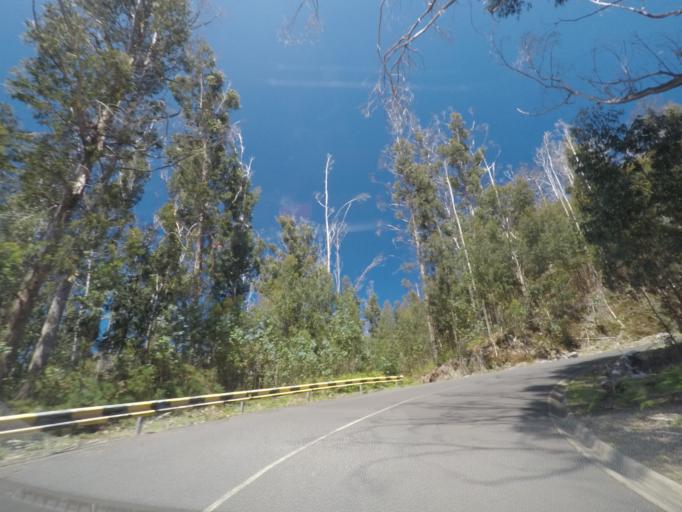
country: PT
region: Madeira
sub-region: Calheta
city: Arco da Calheta
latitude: 32.7379
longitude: -17.1318
